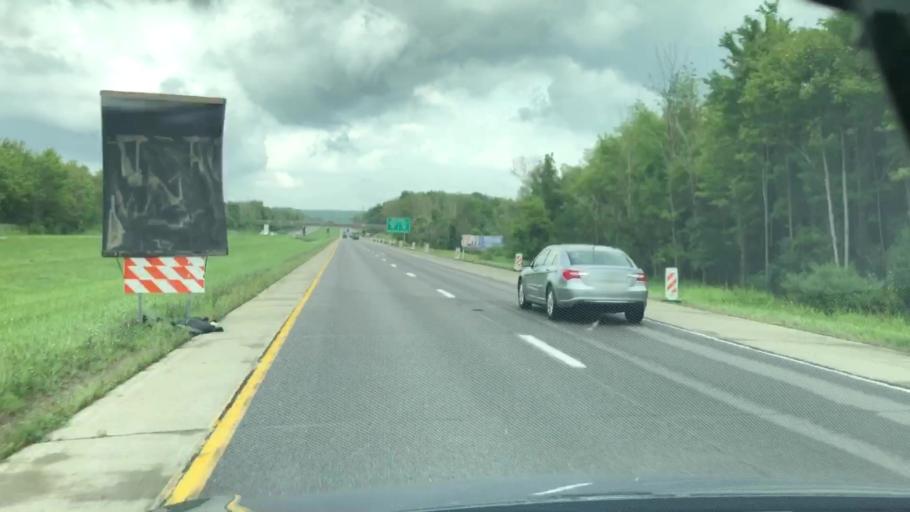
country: US
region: Pennsylvania
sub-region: Erie County
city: Fairview
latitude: 42.0142
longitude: -80.1470
